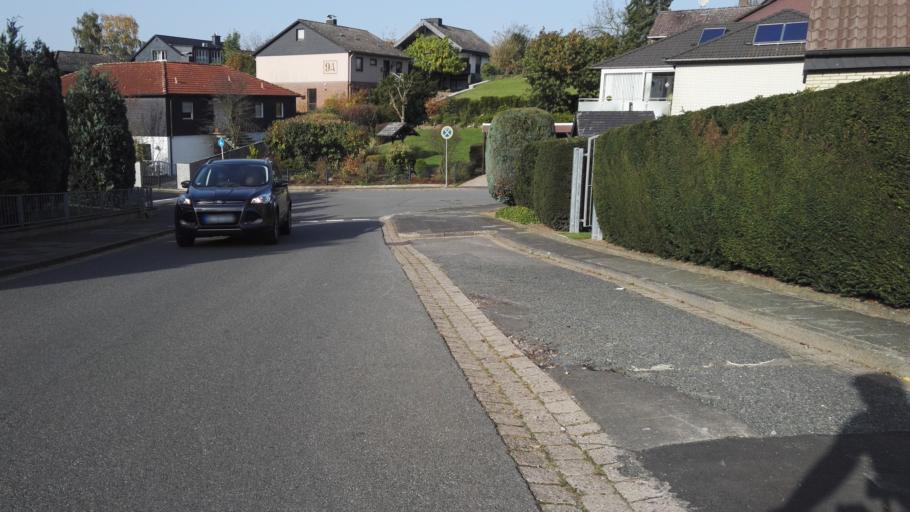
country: DE
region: Lower Saxony
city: Bad Salzdetfurth
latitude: 52.1139
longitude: 10.0001
